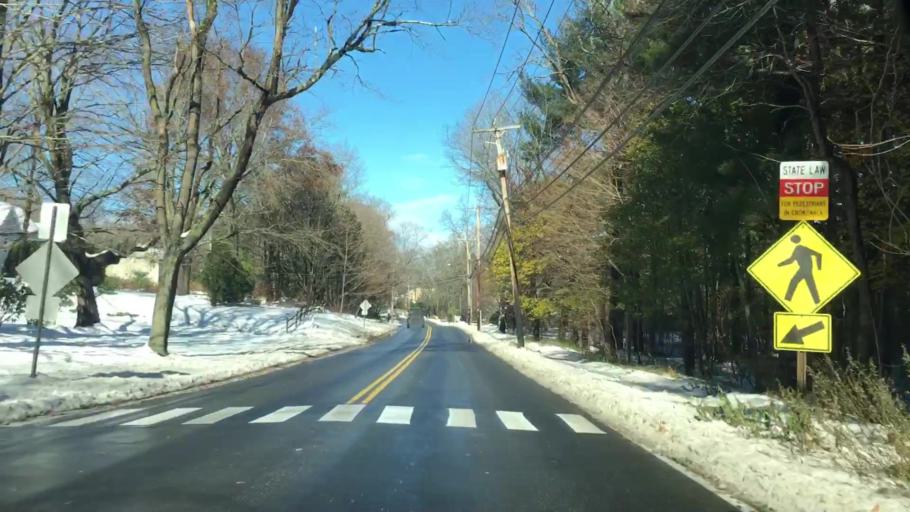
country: US
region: Connecticut
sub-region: Fairfield County
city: Shelton
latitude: 41.2866
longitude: -73.1399
